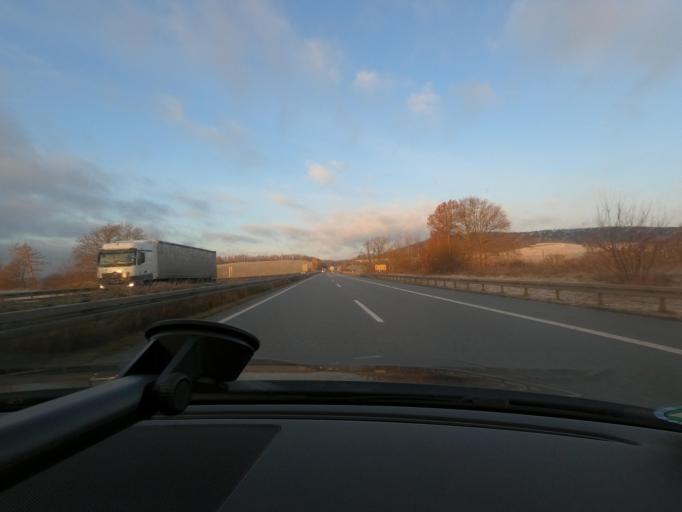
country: DE
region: Thuringia
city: Rohrberg
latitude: 51.3999
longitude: 10.0274
